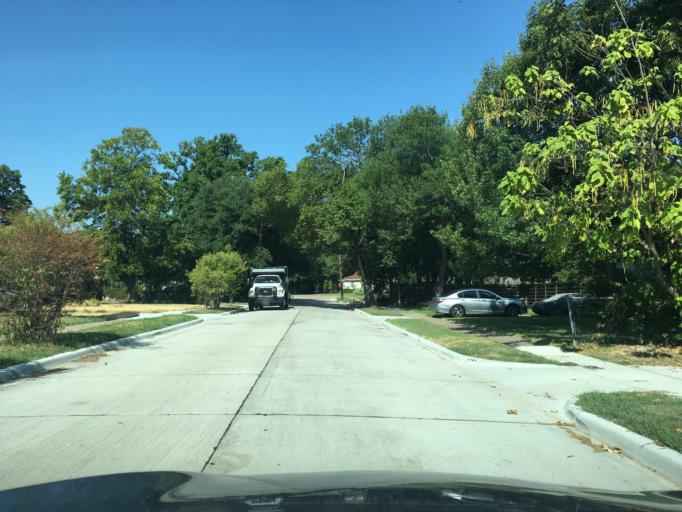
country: US
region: Texas
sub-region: Dallas County
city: Garland
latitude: 32.8524
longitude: -96.6752
